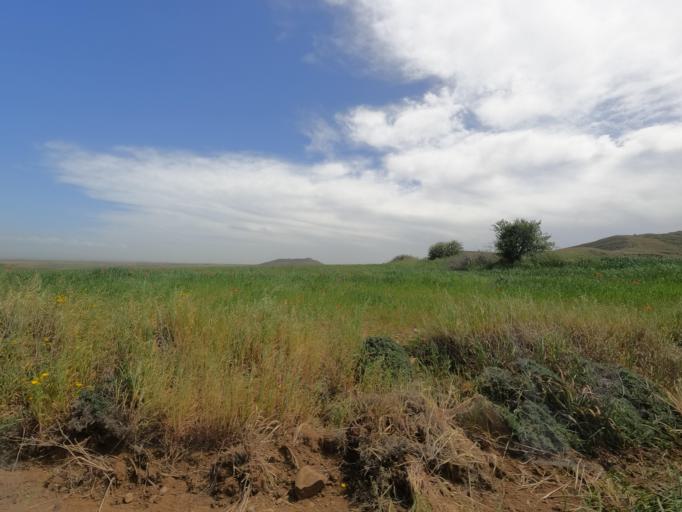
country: CY
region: Lefkosia
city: Lefka
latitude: 35.0879
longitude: 32.9279
